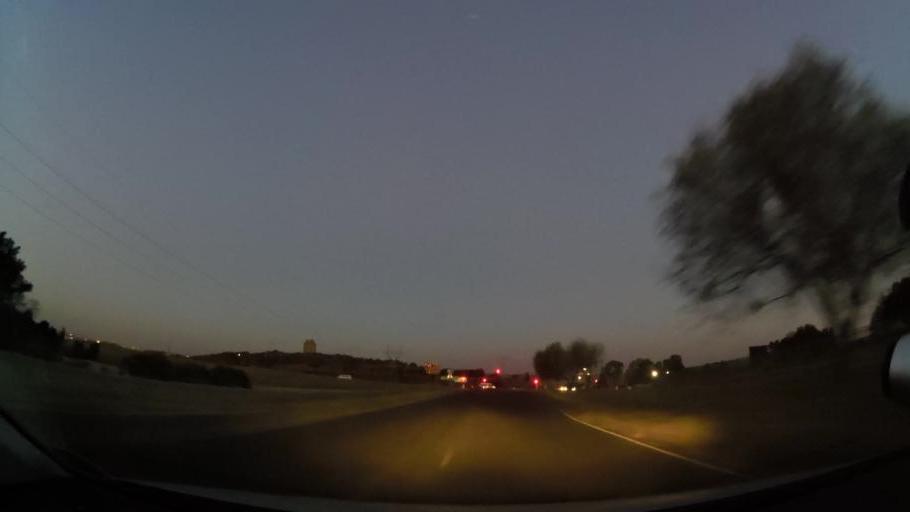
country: ZA
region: Gauteng
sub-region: City of Tshwane Metropolitan Municipality
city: Pretoria
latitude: -25.7759
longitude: 28.1659
